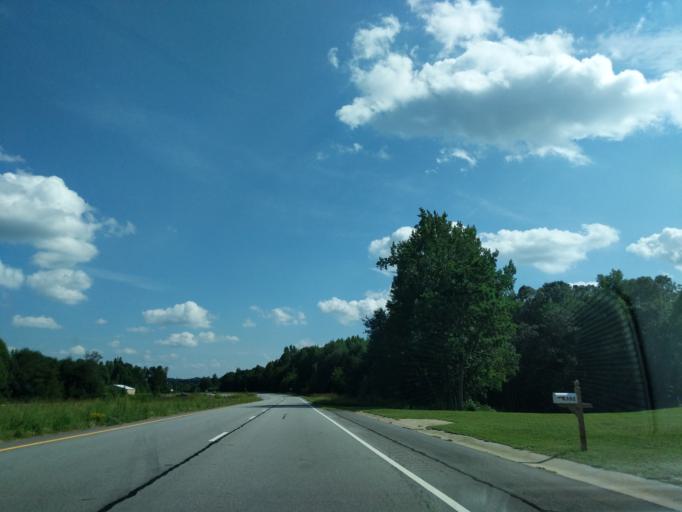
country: US
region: Georgia
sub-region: Habersham County
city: Baldwin
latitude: 34.4339
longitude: -83.5054
